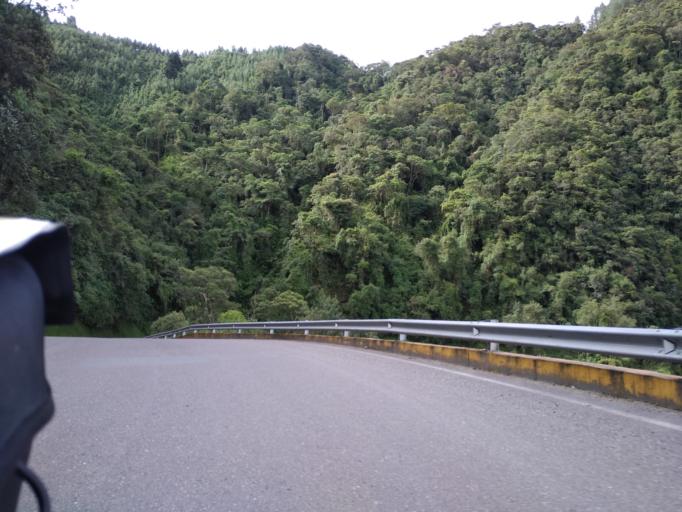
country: CO
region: Tolima
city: Herveo
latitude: 5.1227
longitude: -75.2032
